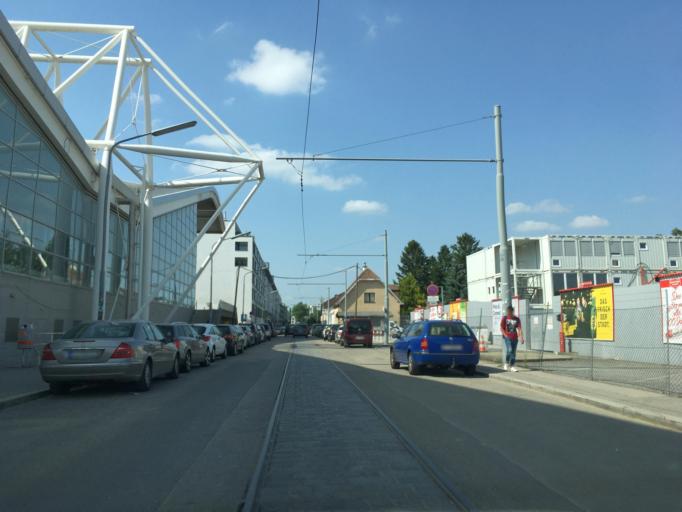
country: AT
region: Lower Austria
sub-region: Politischer Bezirk Wien-Umgebung
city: Gerasdorf bei Wien
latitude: 48.2456
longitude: 16.4342
